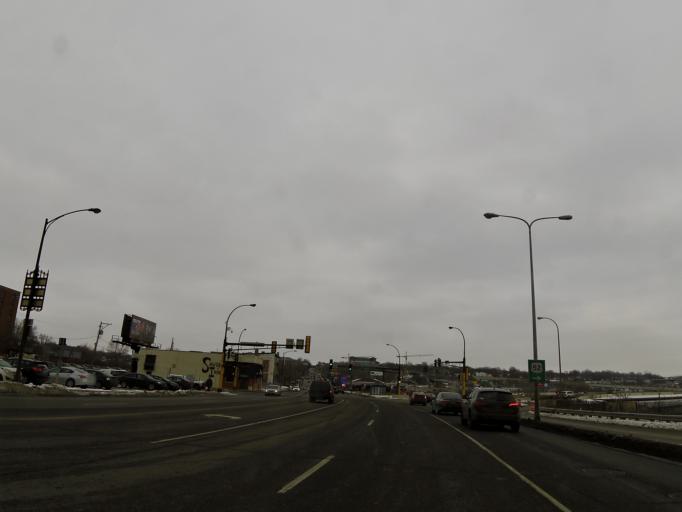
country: US
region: Minnesota
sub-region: Ramsey County
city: Saint Paul
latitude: 44.9530
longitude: -93.0843
